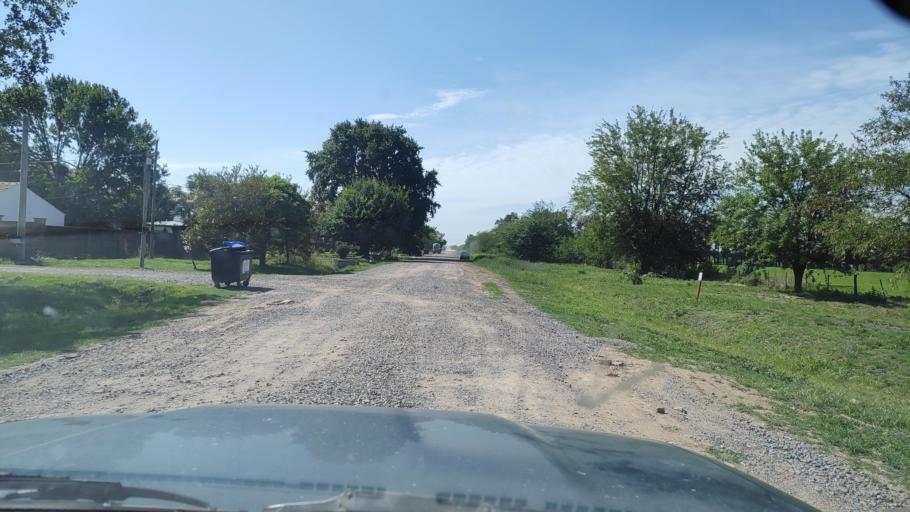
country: AR
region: Buenos Aires
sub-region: Partido de Lujan
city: Lujan
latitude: -34.5448
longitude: -59.1457
